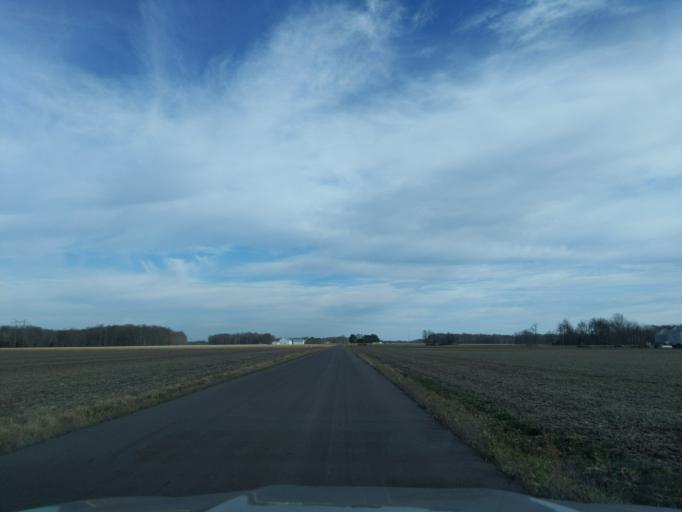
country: US
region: Indiana
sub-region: Decatur County
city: Greensburg
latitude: 39.2341
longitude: -85.4270
